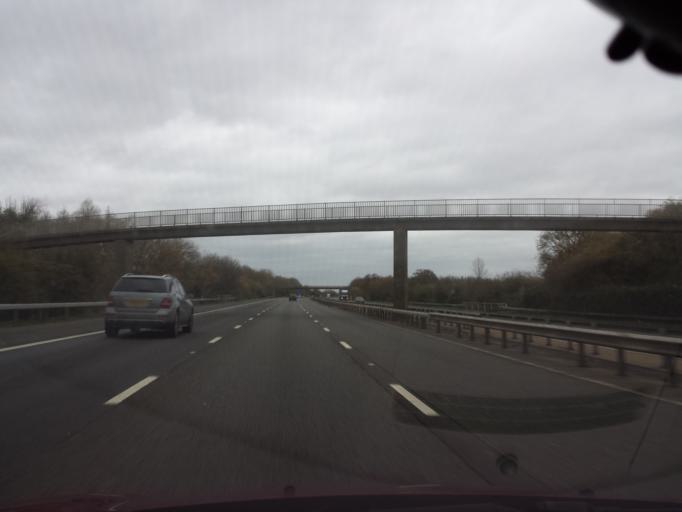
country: GB
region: England
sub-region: Surrey
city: Shepperton
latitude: 51.4030
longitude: -0.4483
